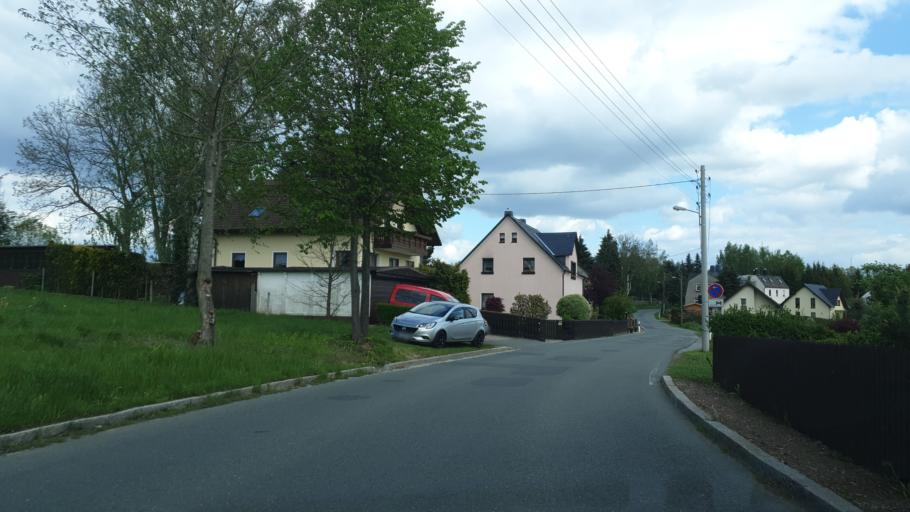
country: DE
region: Saxony
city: Kirchberg
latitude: 50.7792
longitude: 12.7789
